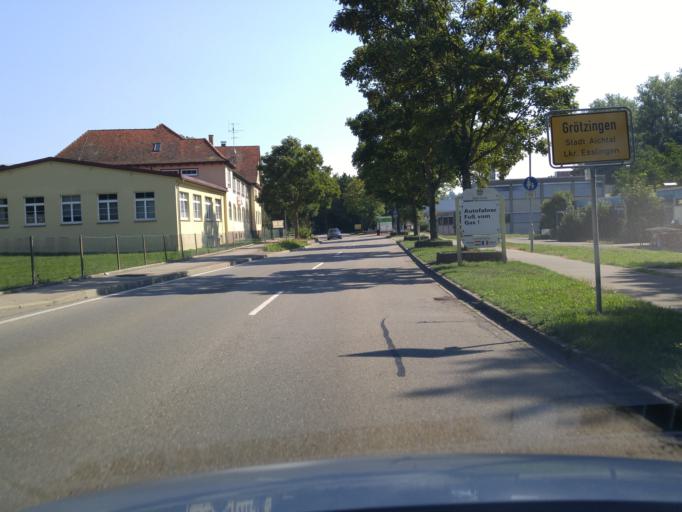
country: DE
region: Baden-Wuerttemberg
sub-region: Regierungsbezirk Stuttgart
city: Neckartailfingen
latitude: 48.6261
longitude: 9.2527
